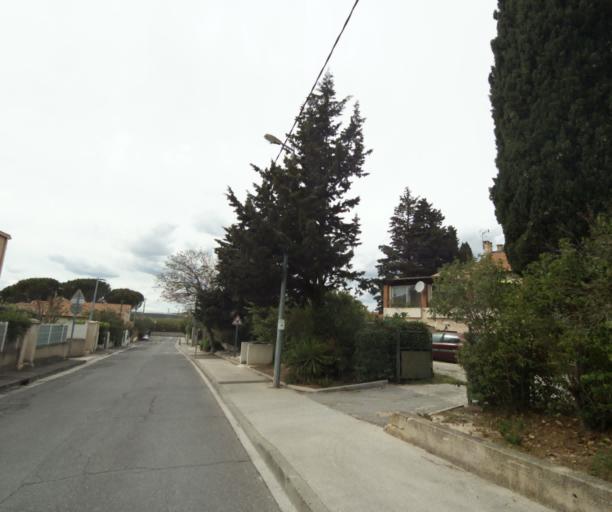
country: FR
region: Provence-Alpes-Cote d'Azur
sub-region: Departement des Bouches-du-Rhone
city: Rognac
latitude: 43.4903
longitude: 5.2329
